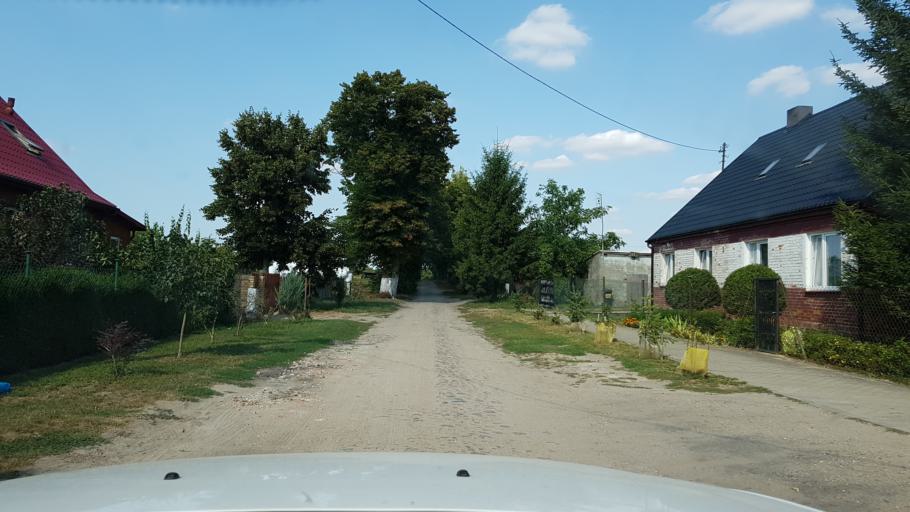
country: PL
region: West Pomeranian Voivodeship
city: Trzcinsko Zdroj
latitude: 52.8922
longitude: 14.5282
